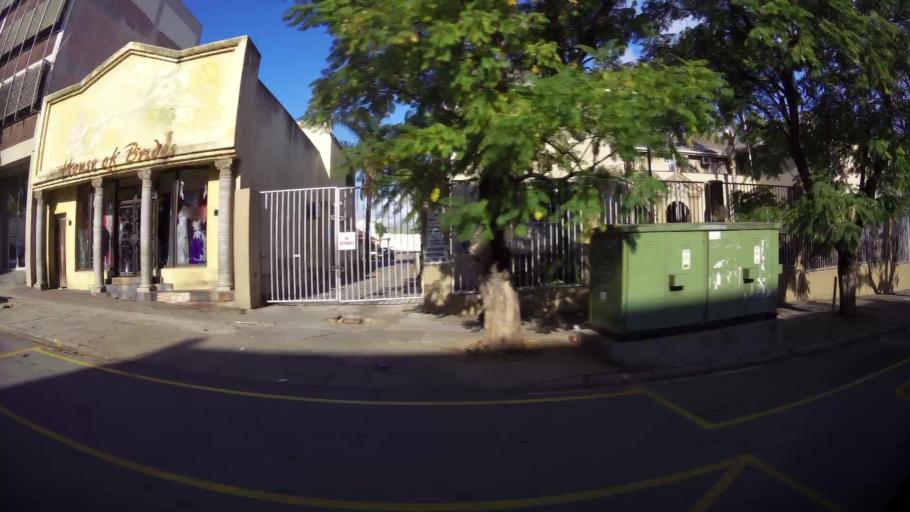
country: ZA
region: Eastern Cape
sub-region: Nelson Mandela Bay Metropolitan Municipality
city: Uitenhage
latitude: -33.7654
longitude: 25.4006
